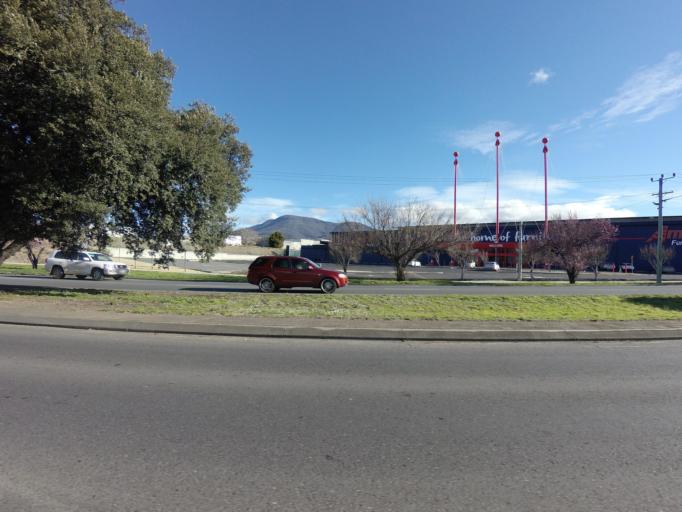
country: AU
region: Tasmania
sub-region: Glenorchy
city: Lutana
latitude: -42.8363
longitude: 147.3018
